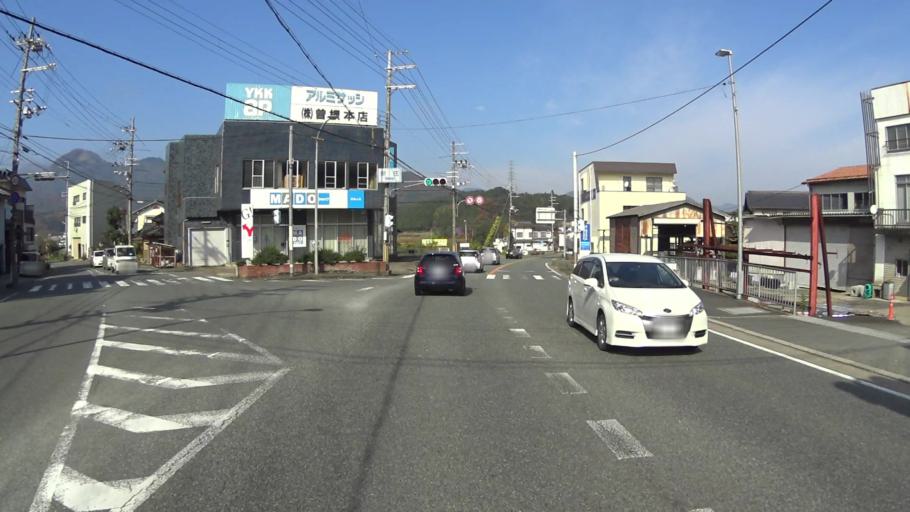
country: JP
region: Kyoto
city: Fukuchiyama
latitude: 35.3051
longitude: 135.1038
